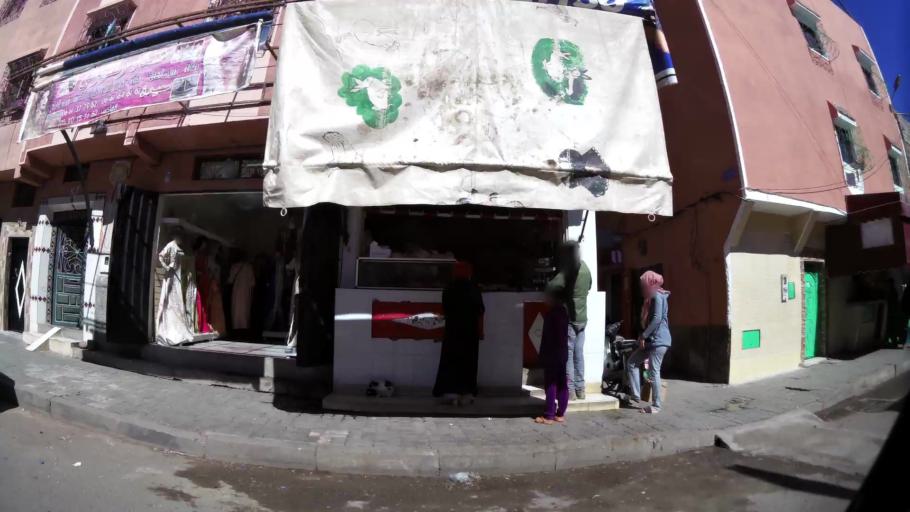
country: MA
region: Marrakech-Tensift-Al Haouz
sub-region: Marrakech
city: Marrakesh
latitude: 31.6479
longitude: -7.9834
